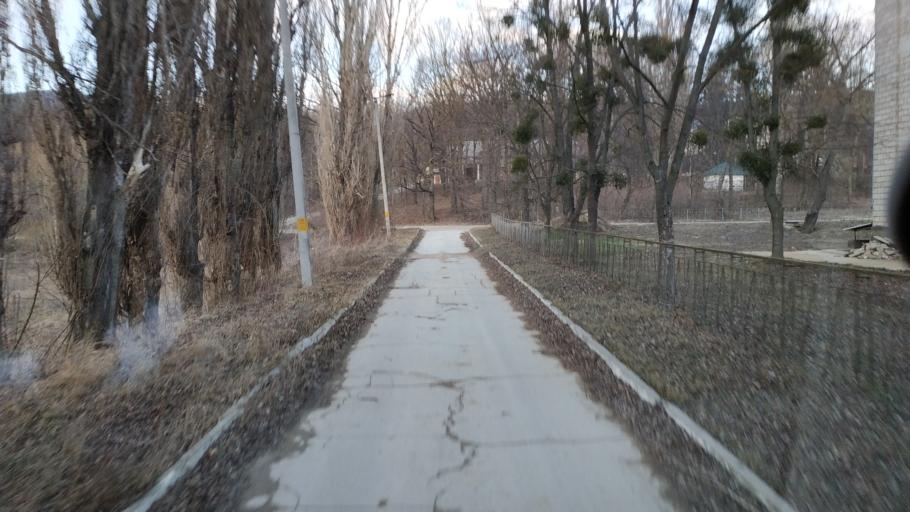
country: MD
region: Calarasi
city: Calarasi
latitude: 47.3301
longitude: 28.2224
